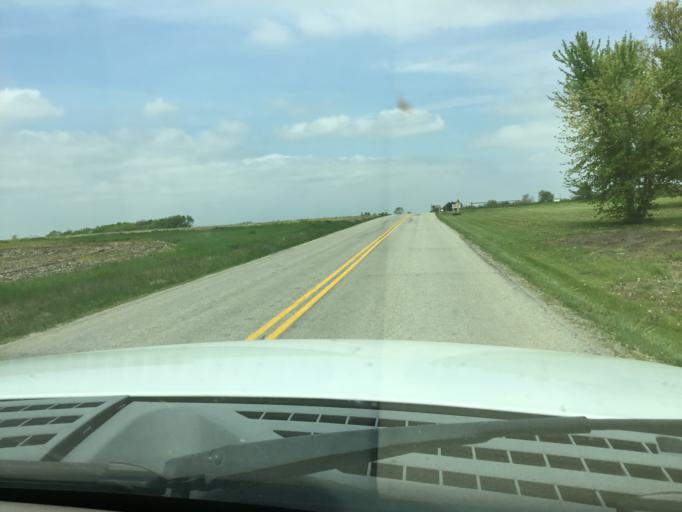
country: US
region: Kansas
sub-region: Shawnee County
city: Topeka
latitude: 38.9591
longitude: -95.6141
